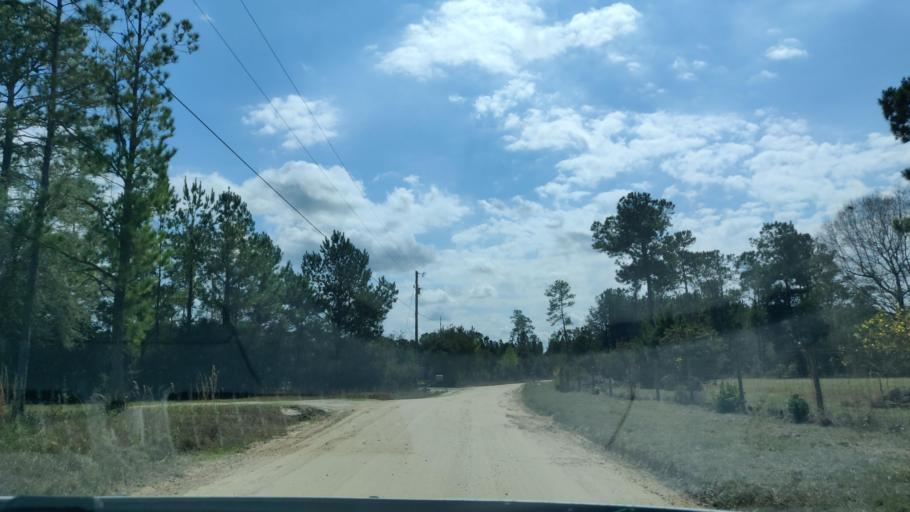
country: US
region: Florida
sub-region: Duval County
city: Baldwin
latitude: 30.1751
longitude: -81.9574
